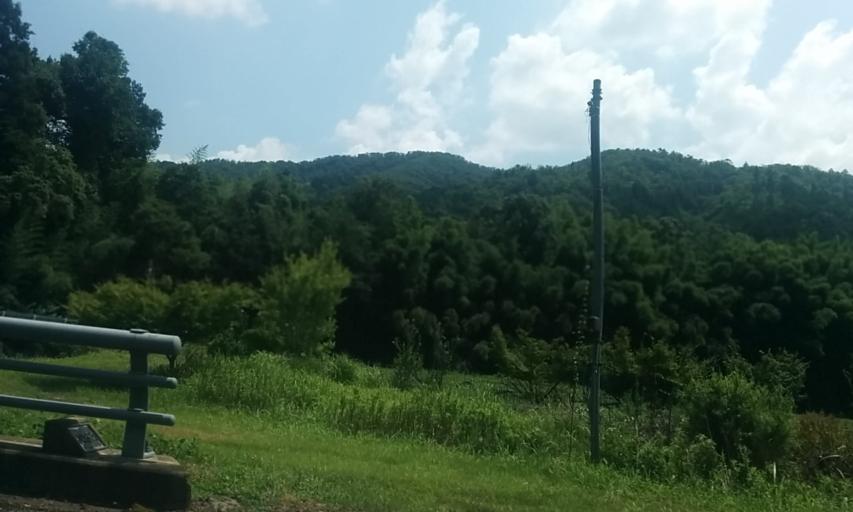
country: JP
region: Kyoto
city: Ayabe
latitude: 35.2123
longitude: 135.2038
